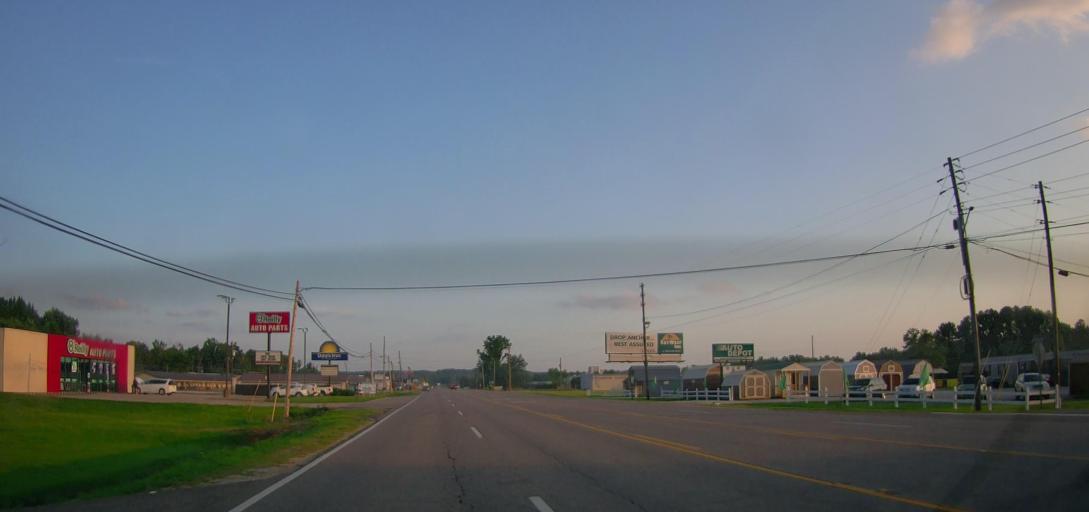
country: US
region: Alabama
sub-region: Marion County
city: Hamilton
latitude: 34.1178
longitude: -87.9895
